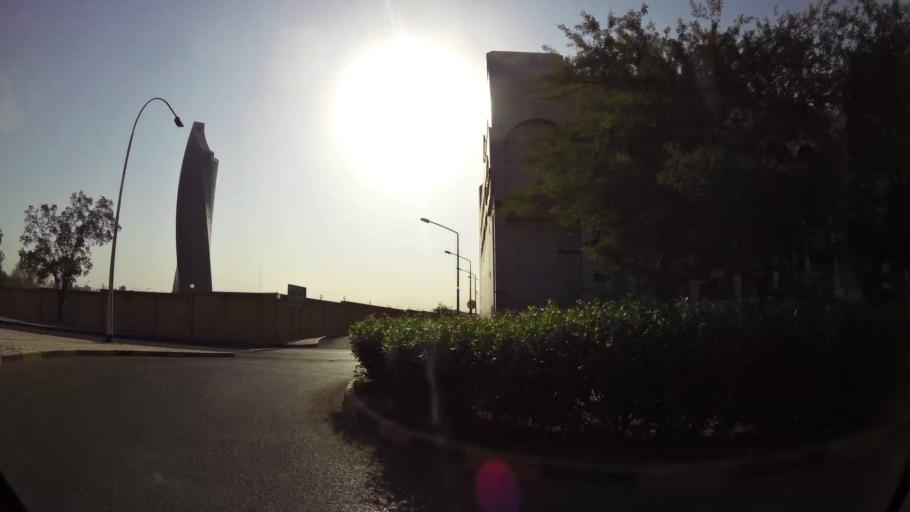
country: KW
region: Al Asimah
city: Kuwait City
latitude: 29.3705
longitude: 47.9874
